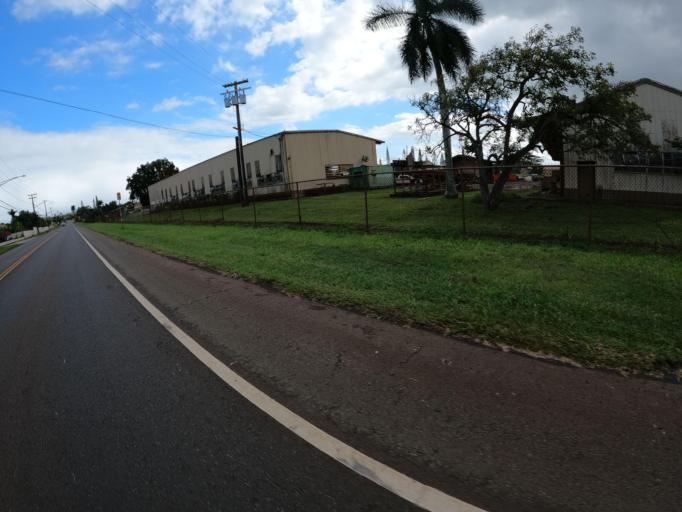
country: US
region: Hawaii
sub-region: Honolulu County
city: Whitmore Village
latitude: 21.5097
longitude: -158.0257
